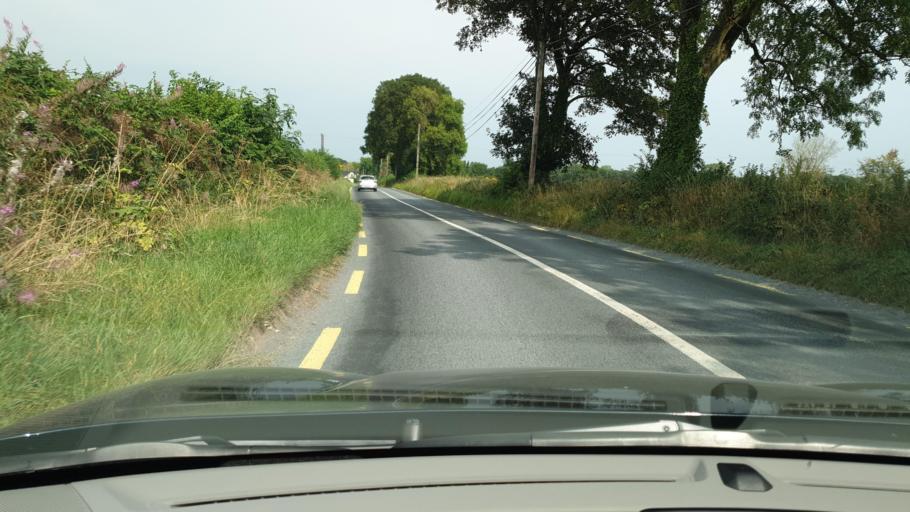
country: IE
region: Leinster
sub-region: An Mhi
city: Athboy
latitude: 53.6439
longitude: -6.8923
